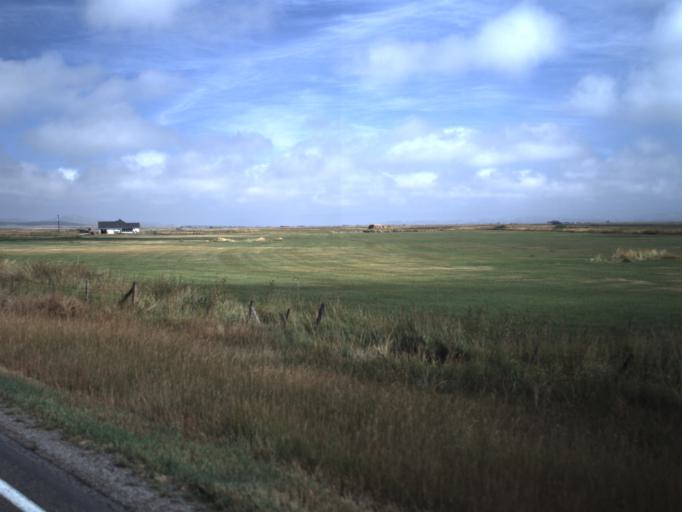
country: US
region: Utah
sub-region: Rich County
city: Randolph
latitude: 41.7105
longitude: -111.1594
